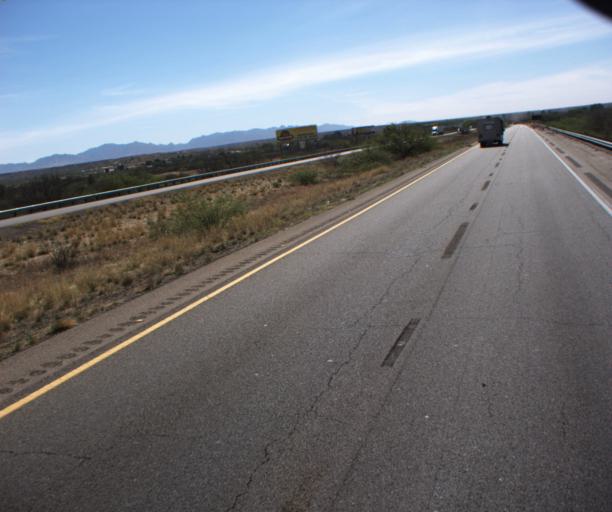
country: US
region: Arizona
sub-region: Cochise County
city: Benson
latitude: 31.9734
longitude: -110.2865
